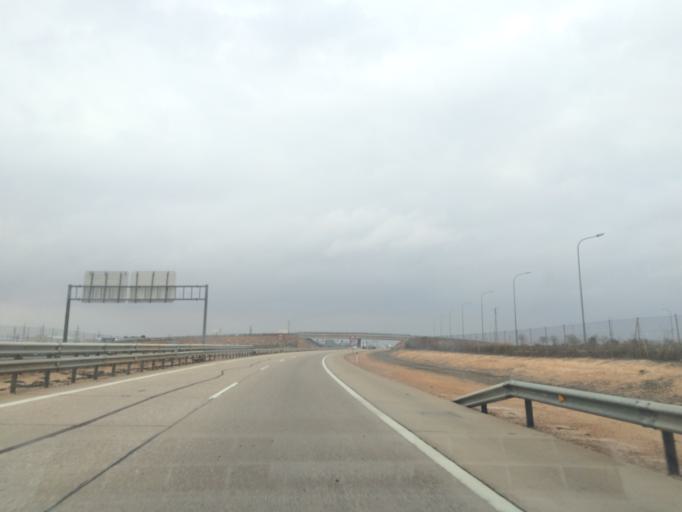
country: ES
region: Castille-La Mancha
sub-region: Province of Toledo
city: Madridejos
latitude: 39.4813
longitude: -3.5245
